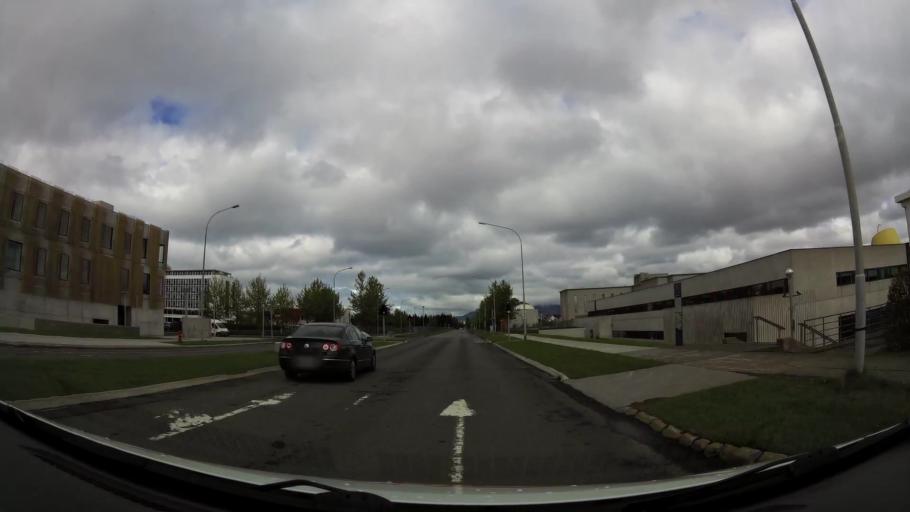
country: IS
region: Capital Region
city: Seltjarnarnes
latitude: 64.1397
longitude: -21.9517
